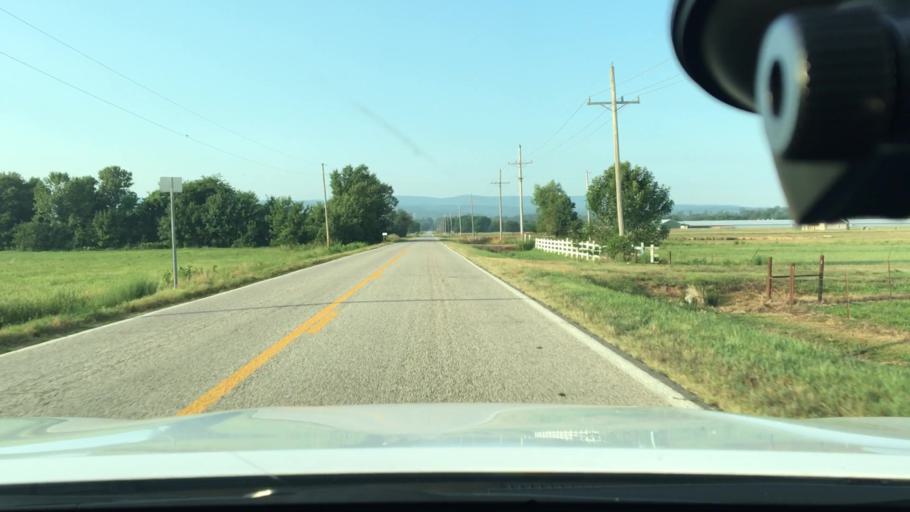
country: US
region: Arkansas
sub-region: Logan County
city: Paris
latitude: 35.3345
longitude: -93.6319
